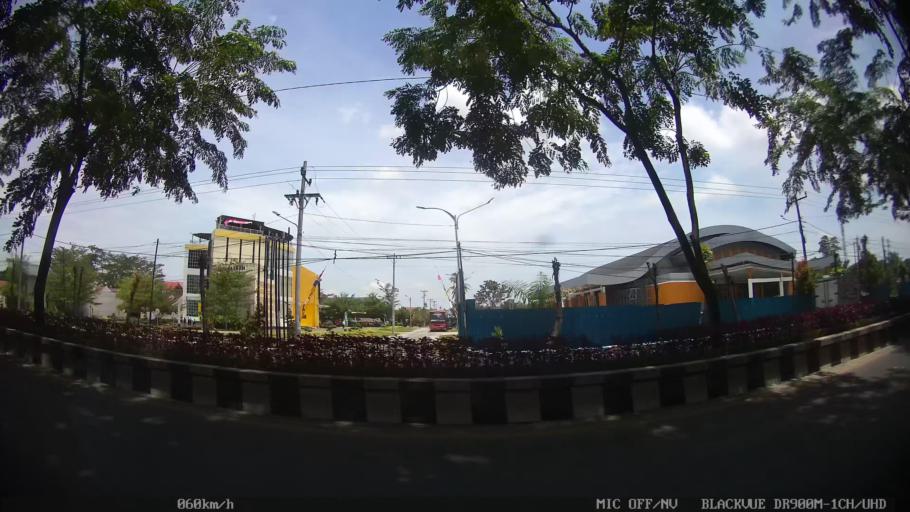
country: ID
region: North Sumatra
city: Percut
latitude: 3.5518
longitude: 98.8665
